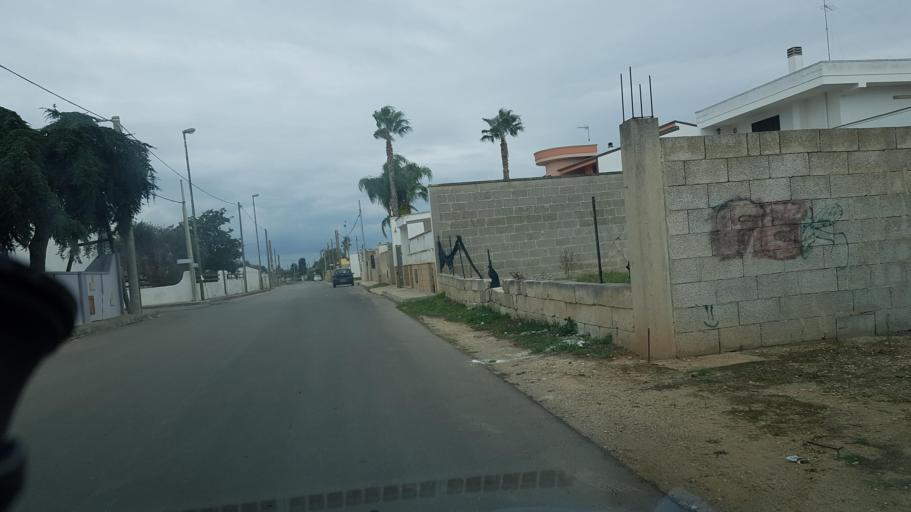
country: IT
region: Apulia
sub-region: Provincia di Lecce
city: Veglie
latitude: 40.3388
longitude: 17.9508
